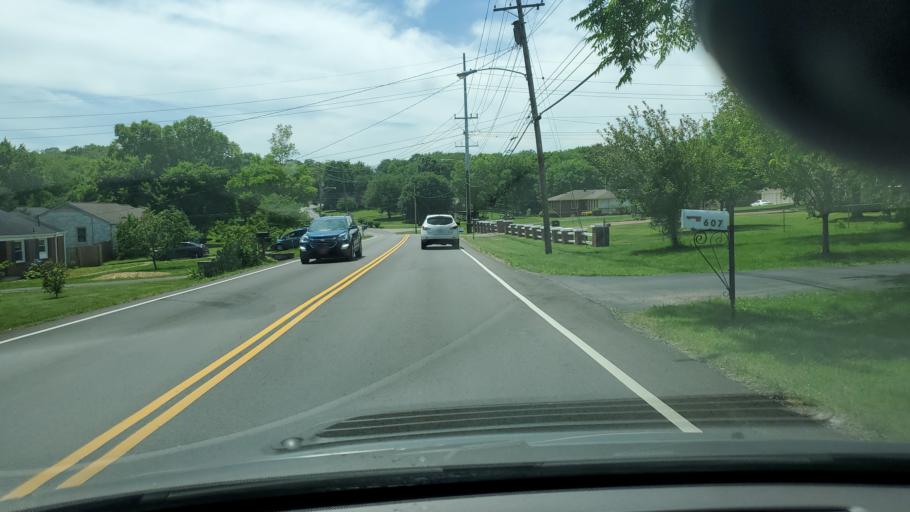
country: US
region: Tennessee
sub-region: Davidson County
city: Nashville
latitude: 36.2298
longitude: -86.7330
